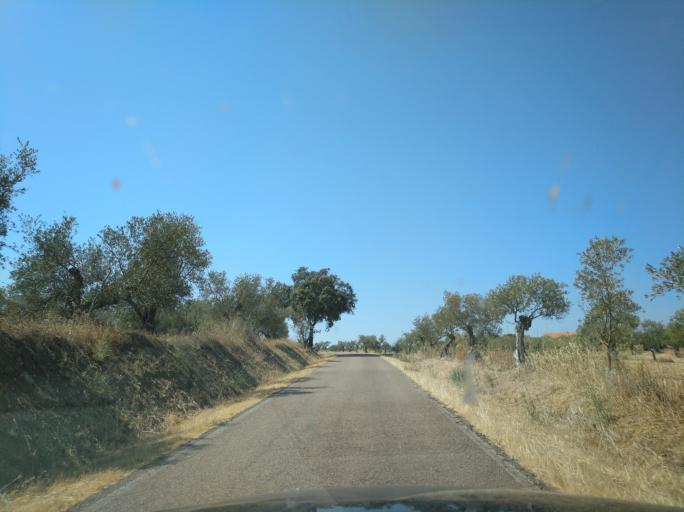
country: PT
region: Portalegre
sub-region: Campo Maior
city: Campo Maior
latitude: 39.0419
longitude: -7.0287
